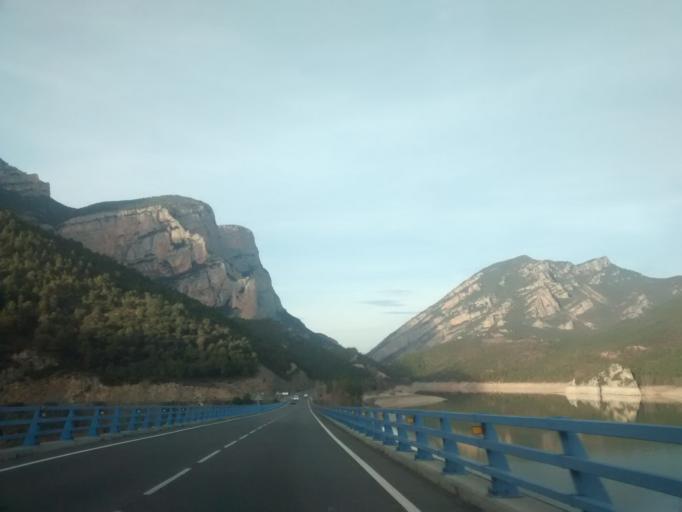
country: ES
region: Catalonia
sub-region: Provincia de Lleida
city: Oliana
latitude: 42.1055
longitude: 1.2989
